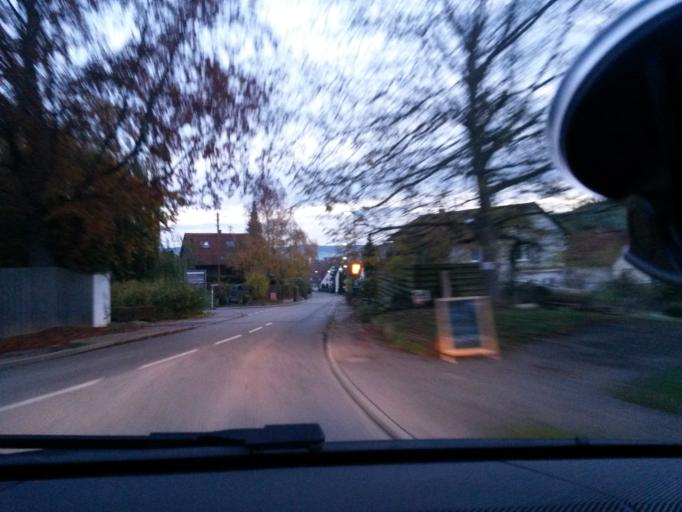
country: DE
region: Baden-Wuerttemberg
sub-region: Regierungsbezirk Stuttgart
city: Weinstadt-Endersbach
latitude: 48.7834
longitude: 9.3349
